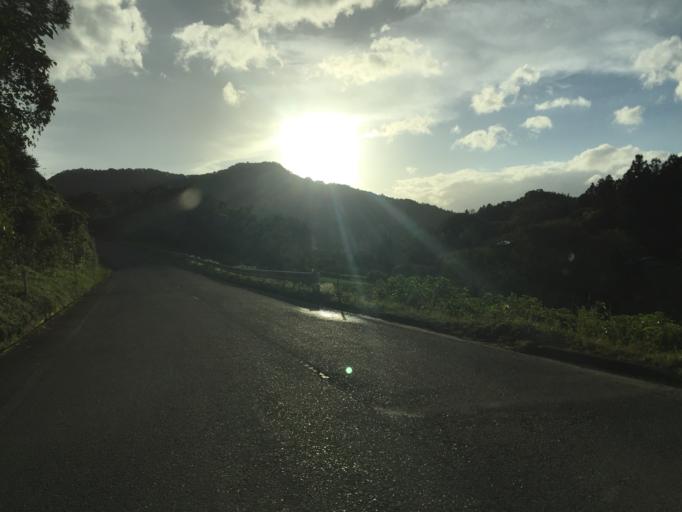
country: JP
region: Fukushima
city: Yanagawamachi-saiwaicho
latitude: 37.9124
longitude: 140.6670
